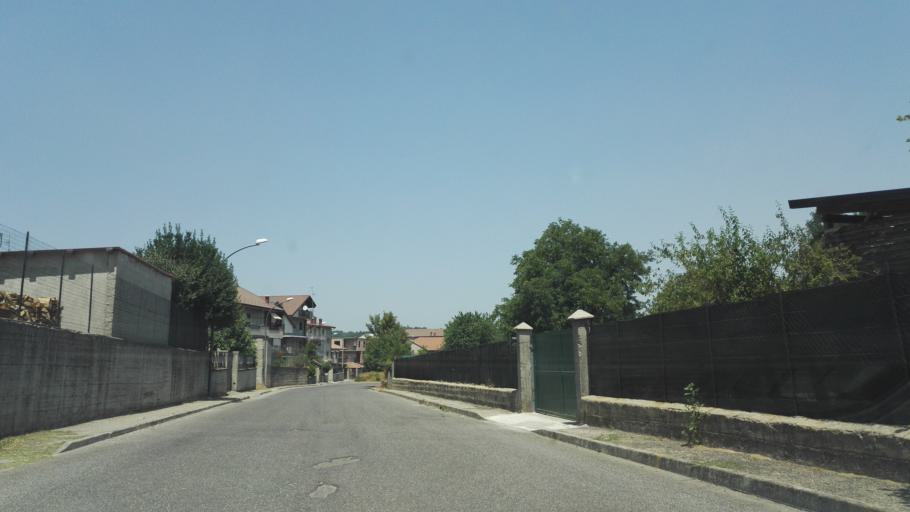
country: IT
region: Calabria
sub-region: Provincia di Vibo-Valentia
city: Serra San Bruno
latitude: 38.5672
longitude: 16.3280
